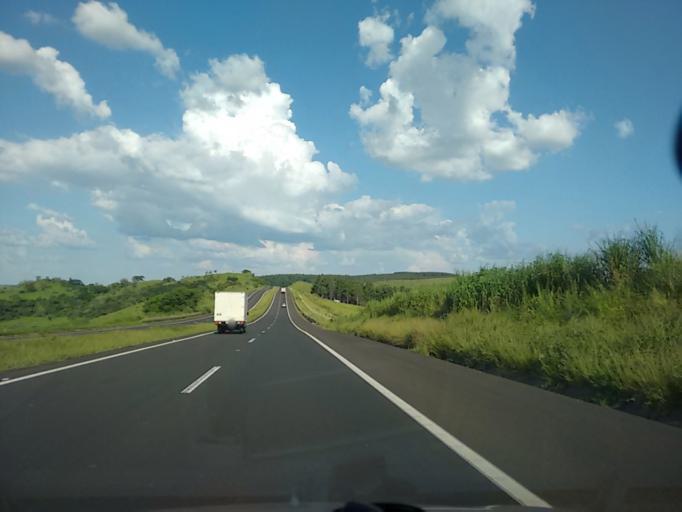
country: BR
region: Sao Paulo
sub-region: Duartina
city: Duartina
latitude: -22.3187
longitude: -49.4906
